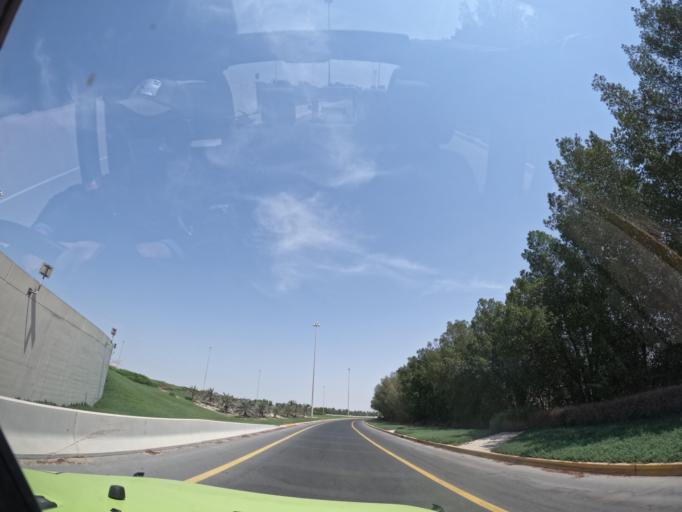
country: AE
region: Abu Dhabi
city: Abu Dhabi
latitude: 24.3280
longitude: 54.5876
